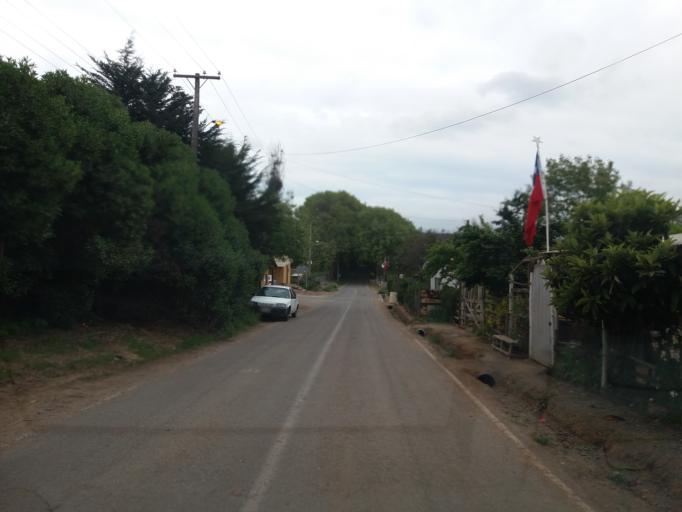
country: CL
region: Valparaiso
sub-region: Provincia de Quillota
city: Quillota
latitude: -32.8924
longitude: -71.3200
